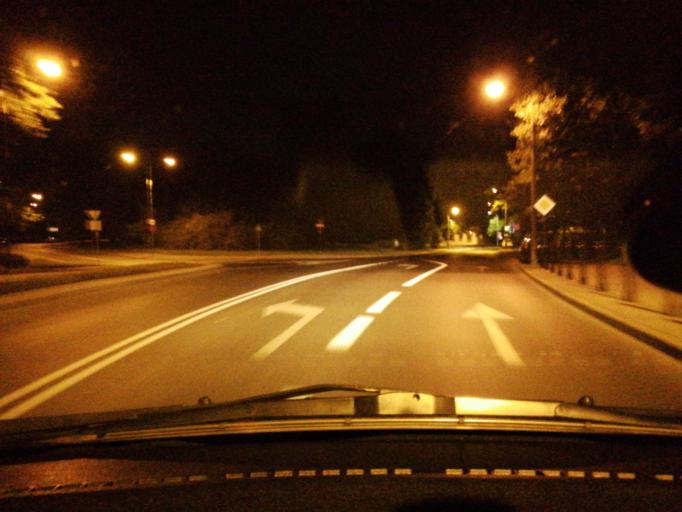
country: PL
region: Masovian Voivodeship
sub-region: Warszawa
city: Zoliborz
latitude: 52.2570
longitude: 21.0047
